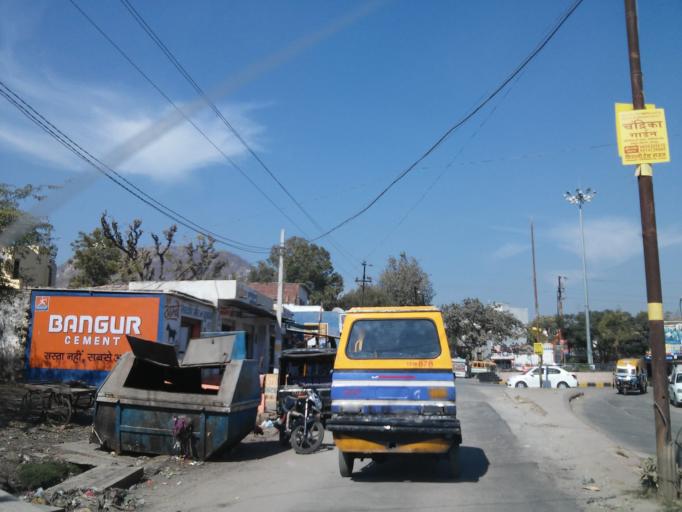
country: IN
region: Rajasthan
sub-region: Udaipur
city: Udaipur
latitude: 24.5831
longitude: 73.6520
